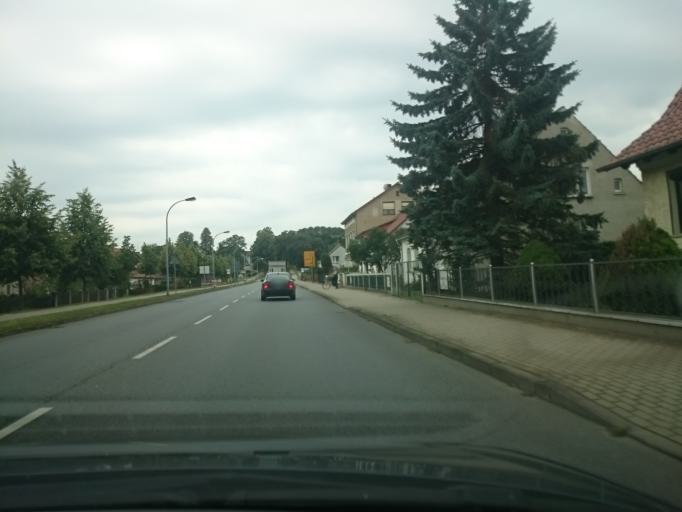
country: DE
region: Brandenburg
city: Furstenberg
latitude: 53.1806
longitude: 13.1442
